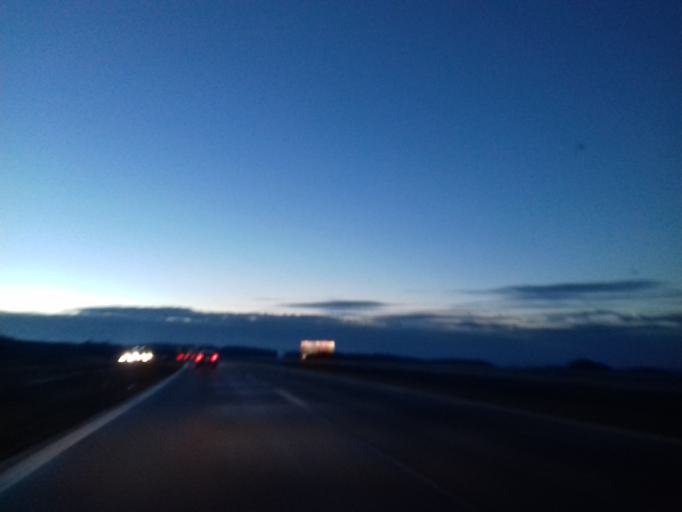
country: CZ
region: Vysocina
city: Krizanov
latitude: 49.3238
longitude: 16.0813
